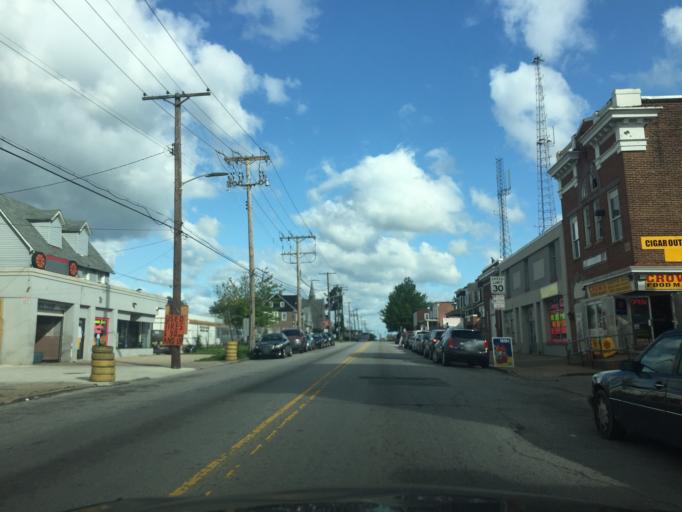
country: US
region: Maryland
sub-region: Baltimore County
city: Lochearn
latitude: 39.3432
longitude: -76.6838
